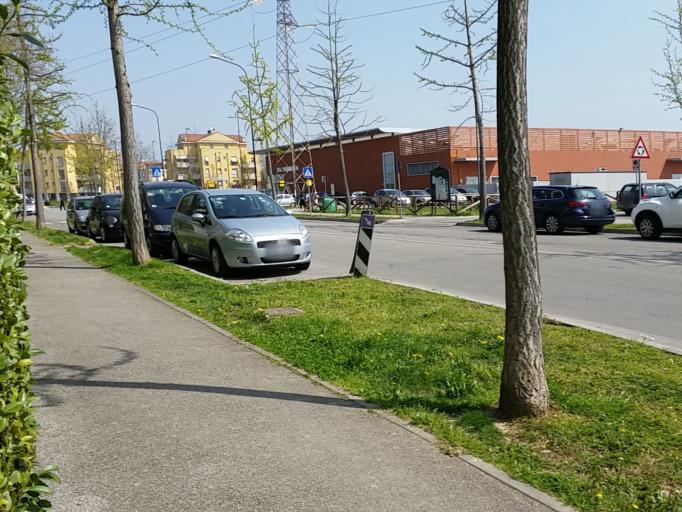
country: IT
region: Veneto
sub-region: Provincia di Padova
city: Mandriola-Sant'Agostino
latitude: 45.3781
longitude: 11.8623
